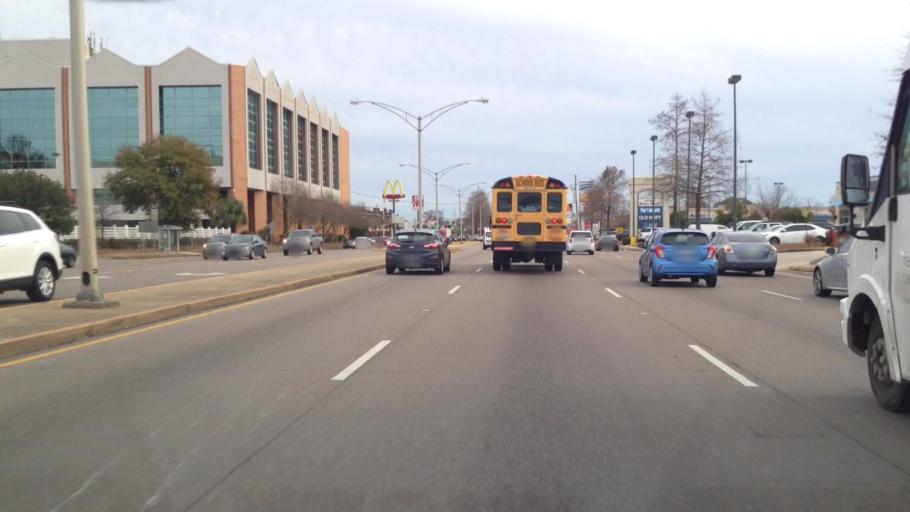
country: US
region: Louisiana
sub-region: Jefferson Parish
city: Elmwood
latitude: 29.9636
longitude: -90.1852
